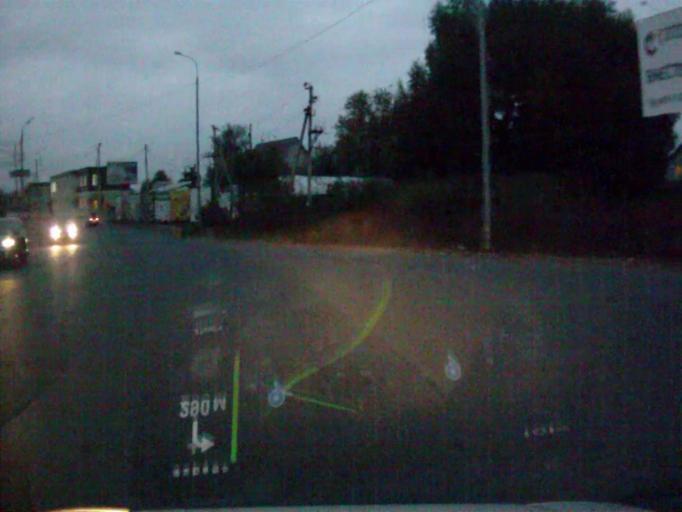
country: RU
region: Chelyabinsk
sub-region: Gorod Chelyabinsk
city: Chelyabinsk
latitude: 55.1564
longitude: 61.2992
